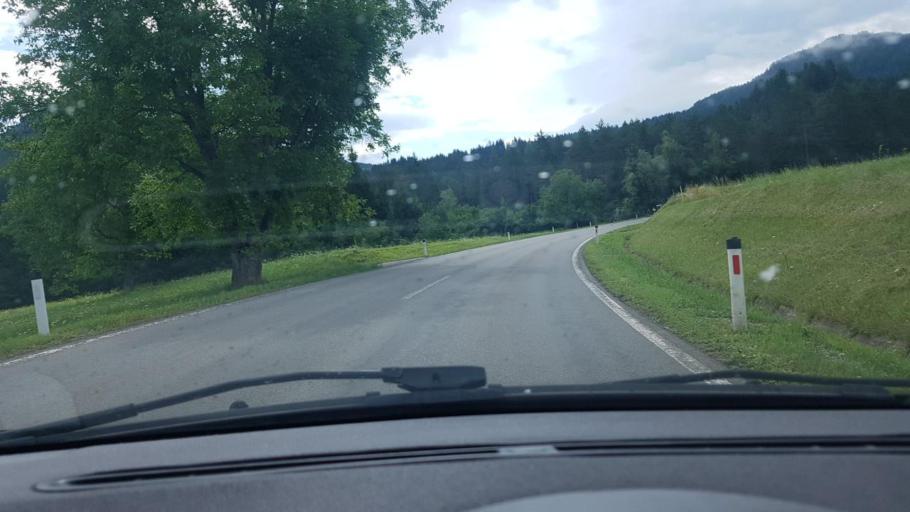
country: AT
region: Carinthia
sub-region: Politischer Bezirk Spittal an der Drau
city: Greifenburg
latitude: 46.7399
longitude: 13.2159
